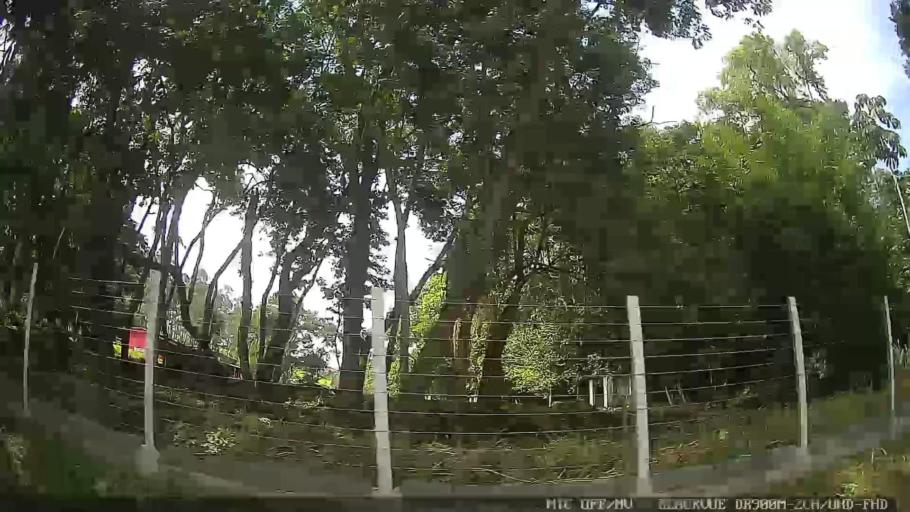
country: BR
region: Sao Paulo
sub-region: Suzano
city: Suzano
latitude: -23.4875
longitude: -46.2720
